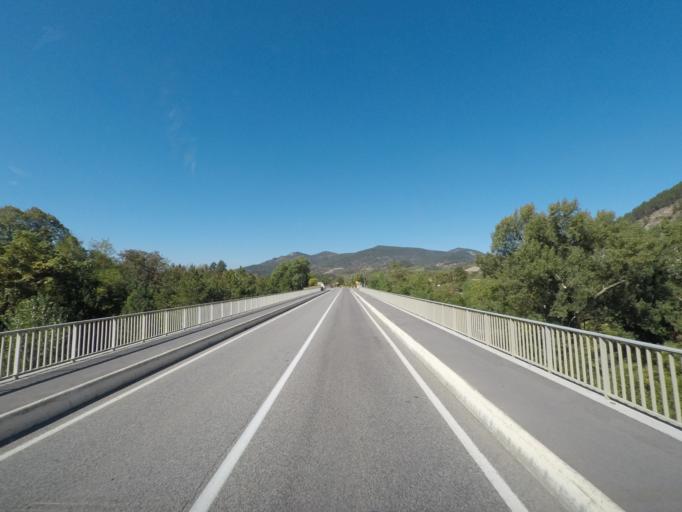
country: FR
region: Rhone-Alpes
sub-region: Departement de la Drome
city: Aouste-sur-Sye
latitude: 44.6934
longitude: 5.2043
